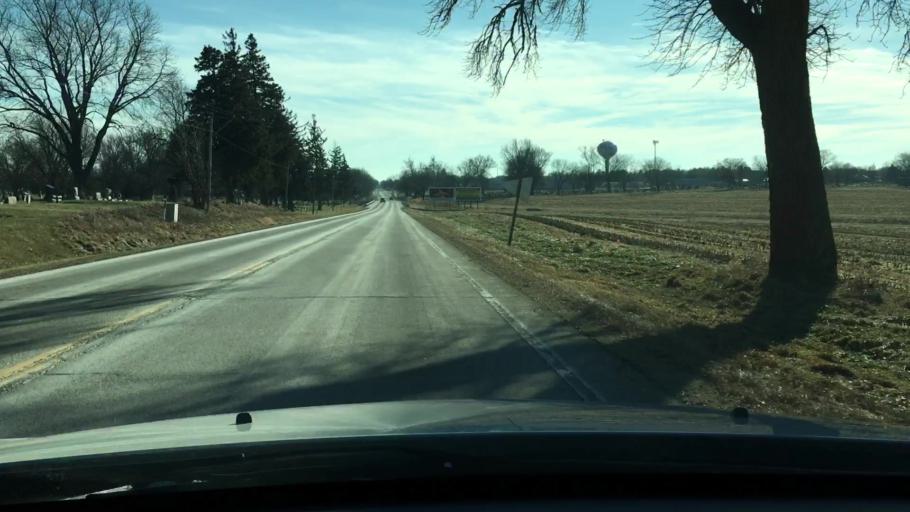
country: US
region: Illinois
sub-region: LaSalle County
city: Mendota
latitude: 41.5682
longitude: -89.1281
